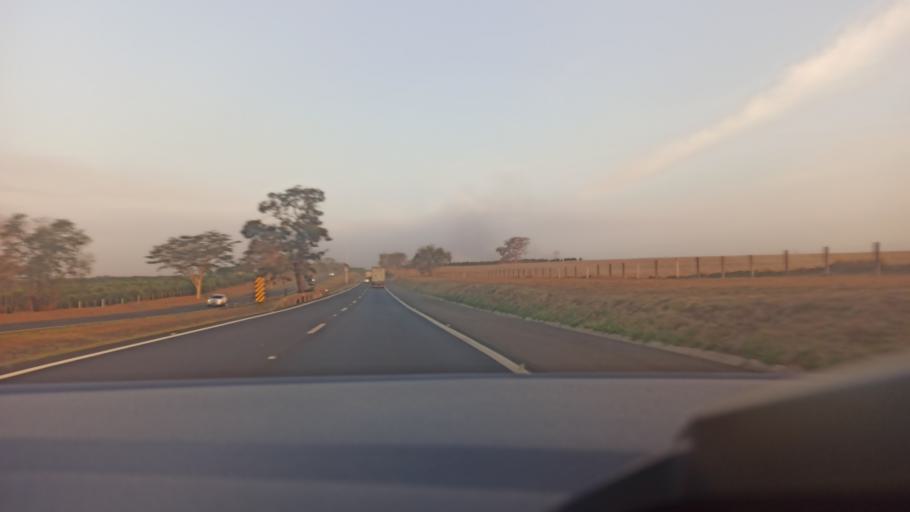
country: BR
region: Sao Paulo
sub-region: Taquaritinga
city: Taquaritinga
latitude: -21.4404
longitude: -48.6498
